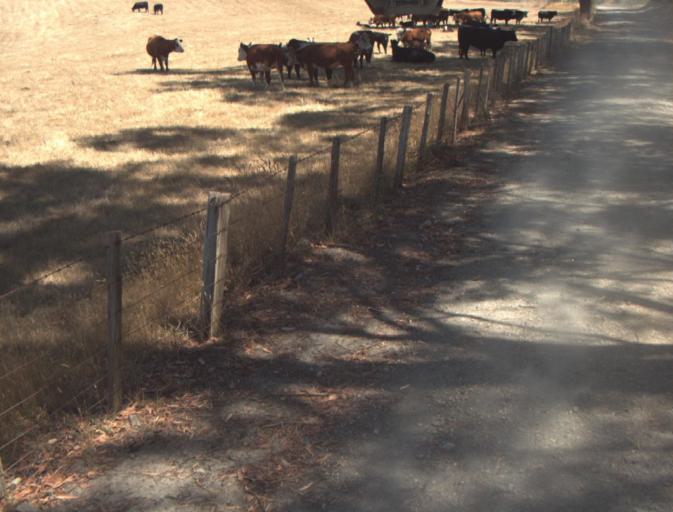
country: AU
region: Tasmania
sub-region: Launceston
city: Mayfield
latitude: -41.2485
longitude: 147.1721
